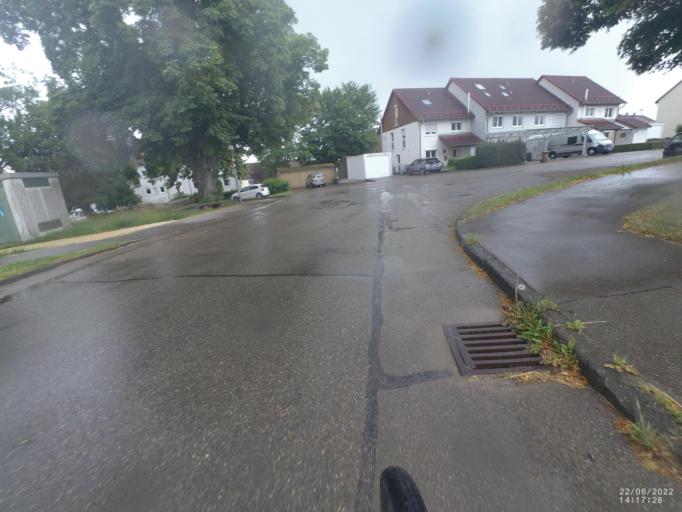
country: DE
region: Baden-Wuerttemberg
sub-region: Regierungsbezirk Stuttgart
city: Gerstetten
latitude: 48.6209
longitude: 10.0334
